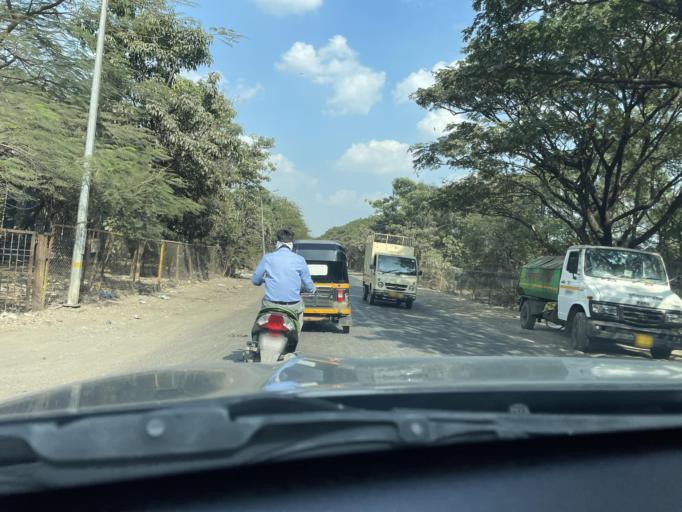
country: IN
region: Maharashtra
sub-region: Pune Division
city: Pune
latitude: 18.5097
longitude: 73.9124
